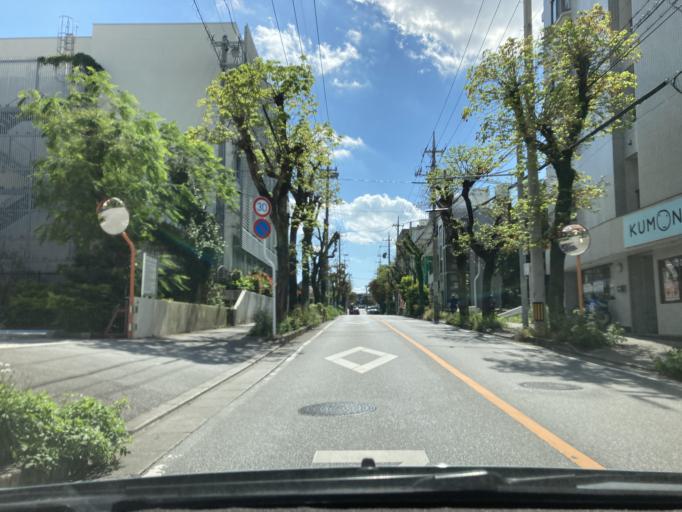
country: JP
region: Okinawa
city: Naha-shi
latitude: 26.2092
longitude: 127.6859
